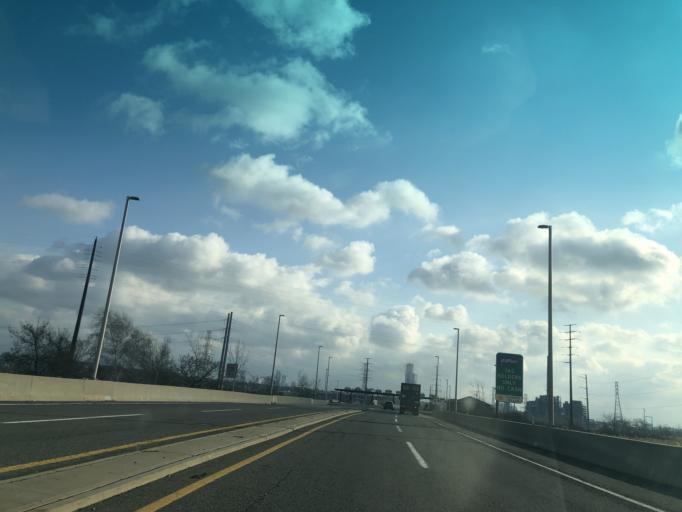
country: US
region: New Jersey
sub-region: Hudson County
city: Jersey City
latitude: 40.7593
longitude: -74.0751
